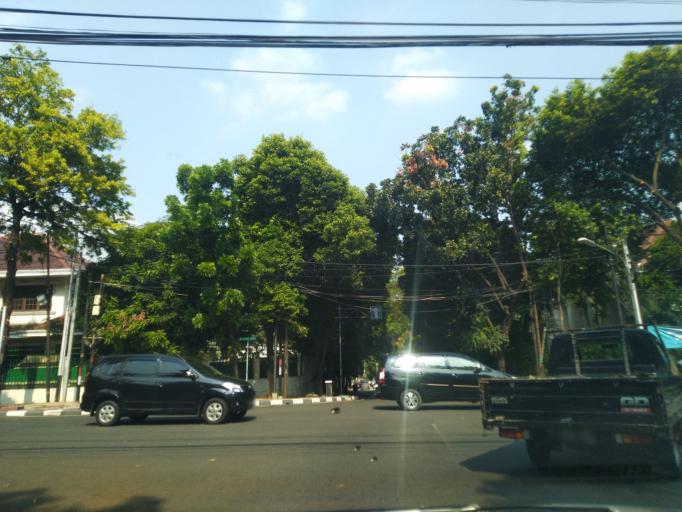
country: ID
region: Jakarta Raya
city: Jakarta
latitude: -6.2368
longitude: 106.7963
